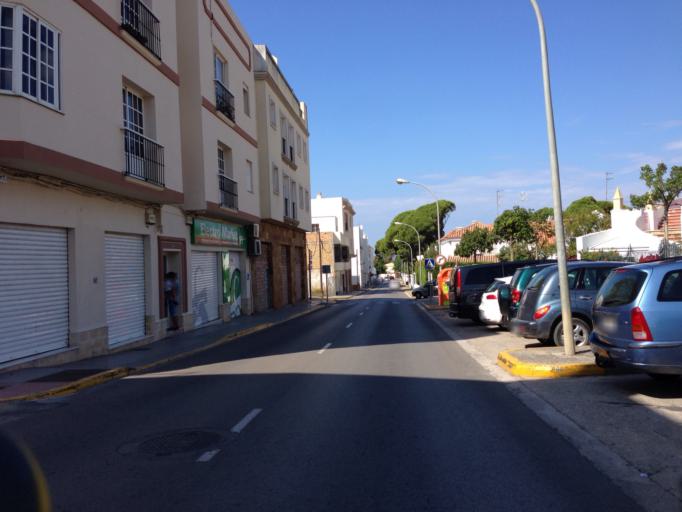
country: ES
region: Andalusia
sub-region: Provincia de Cadiz
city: Chiclana de la Frontera
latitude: 36.4162
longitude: -6.1531
